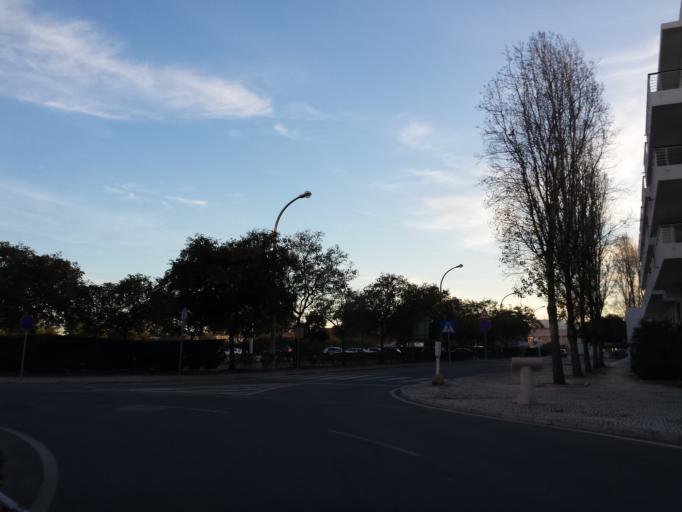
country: PT
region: Faro
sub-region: Lagos
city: Lagos
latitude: 37.1115
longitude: -8.6721
